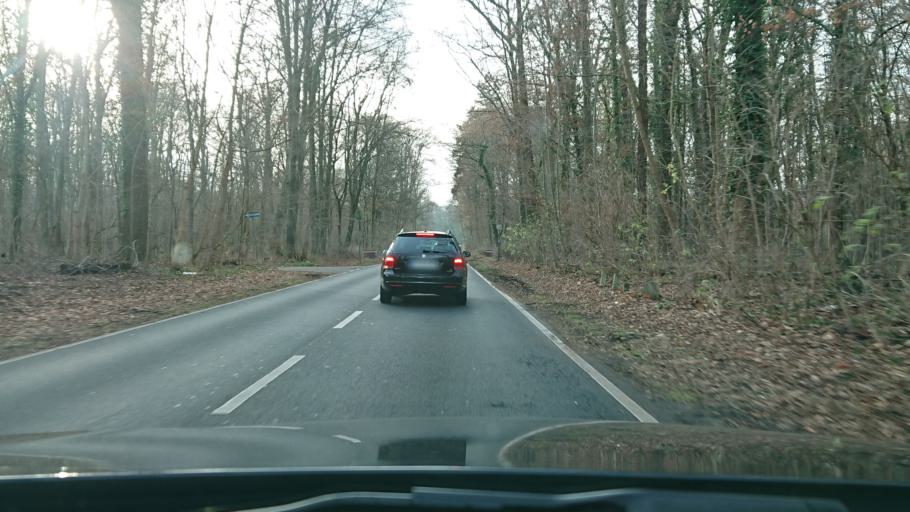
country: DE
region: North Rhine-Westphalia
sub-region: Regierungsbezirk Koln
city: Hurth
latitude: 50.9142
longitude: 6.8948
